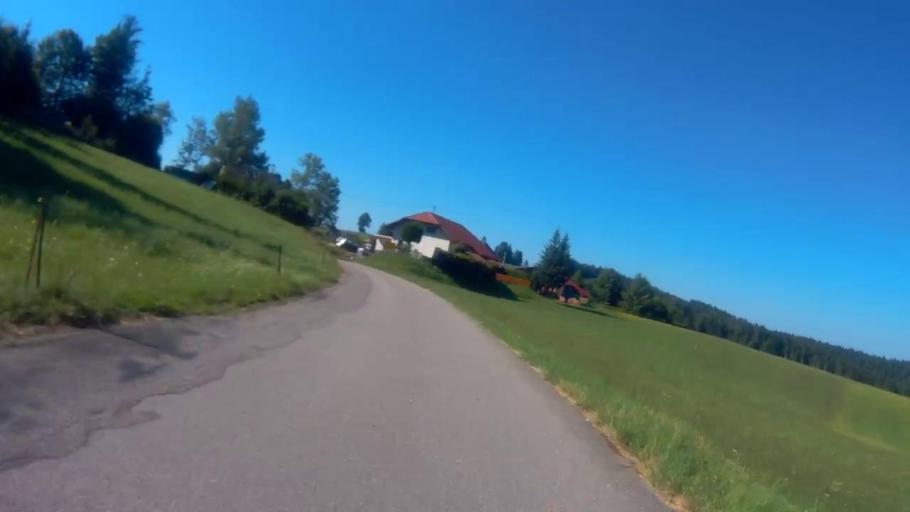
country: DE
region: Baden-Wuerttemberg
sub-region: Freiburg Region
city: Wembach
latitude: 47.7459
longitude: 7.9061
